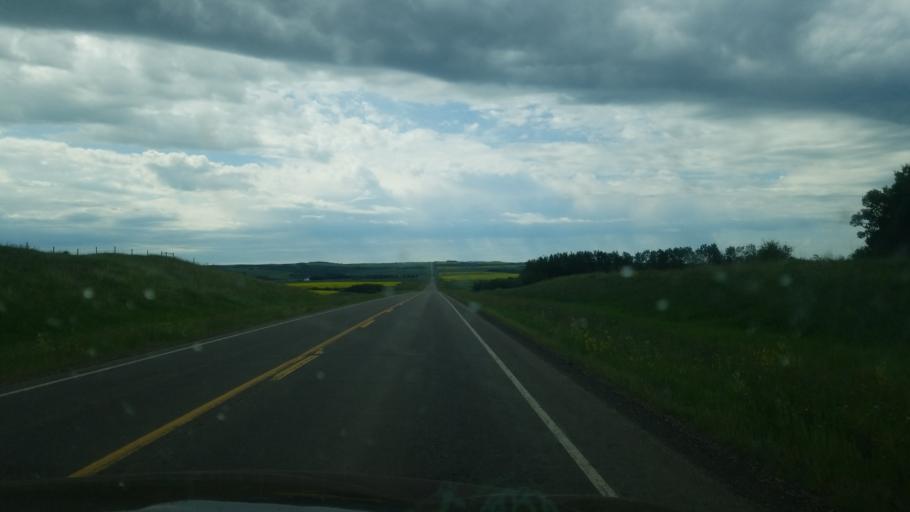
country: CA
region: Saskatchewan
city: Unity
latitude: 52.9215
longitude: -109.3426
